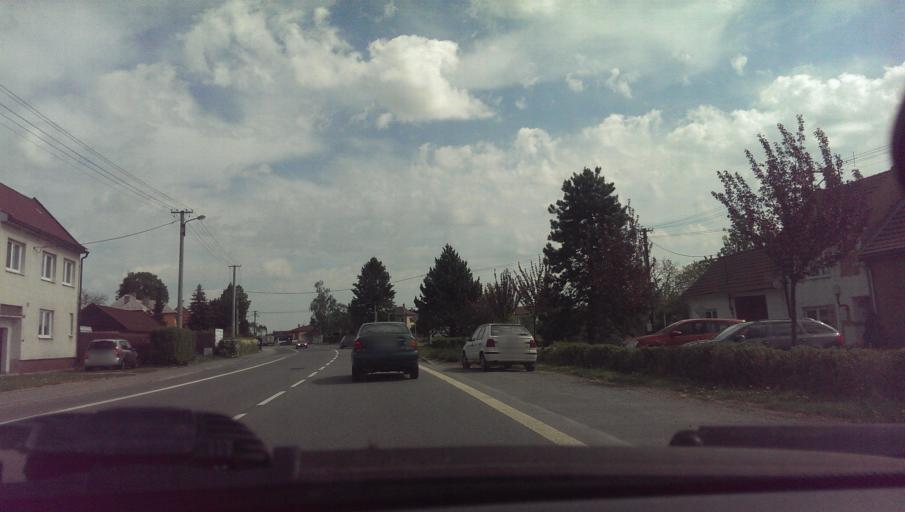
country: CZ
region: Zlin
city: Babice
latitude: 49.1202
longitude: 17.4736
